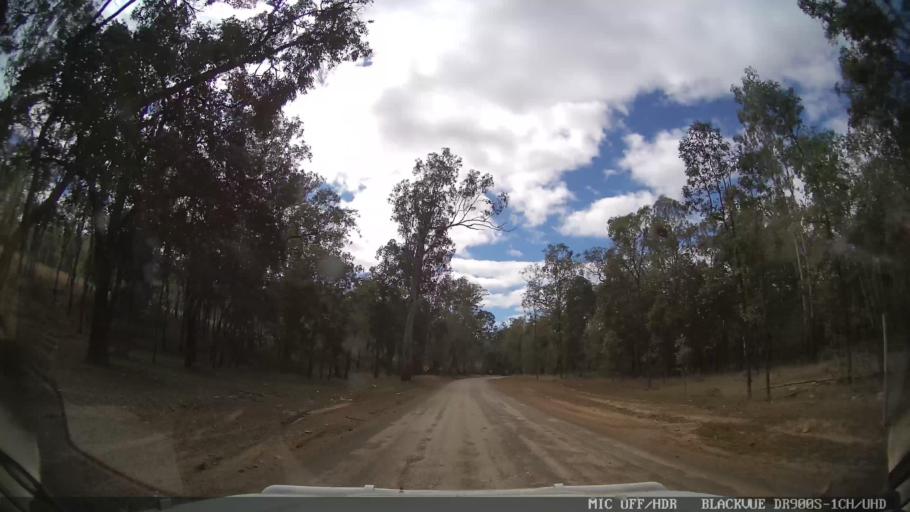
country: AU
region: Queensland
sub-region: Gladstone
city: Toolooa
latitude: -24.5485
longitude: 151.3434
